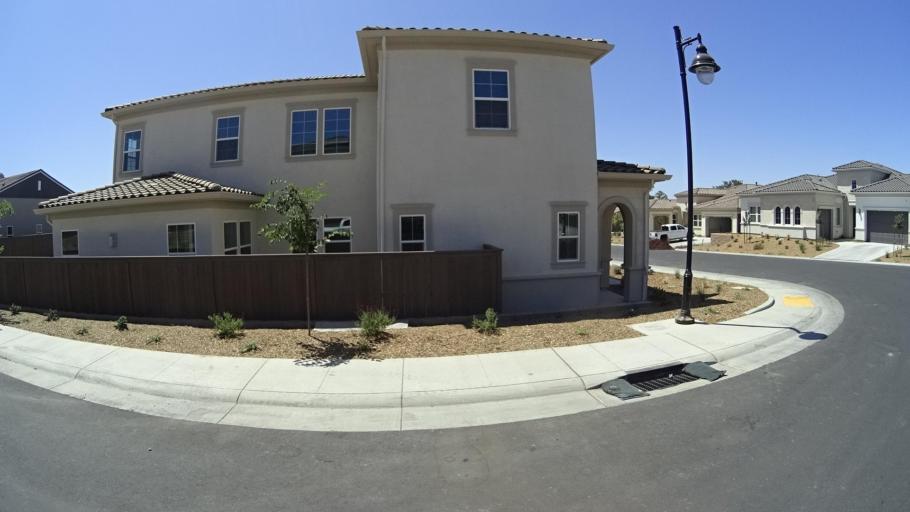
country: US
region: California
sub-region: Placer County
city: Rocklin
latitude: 38.8364
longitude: -121.2513
